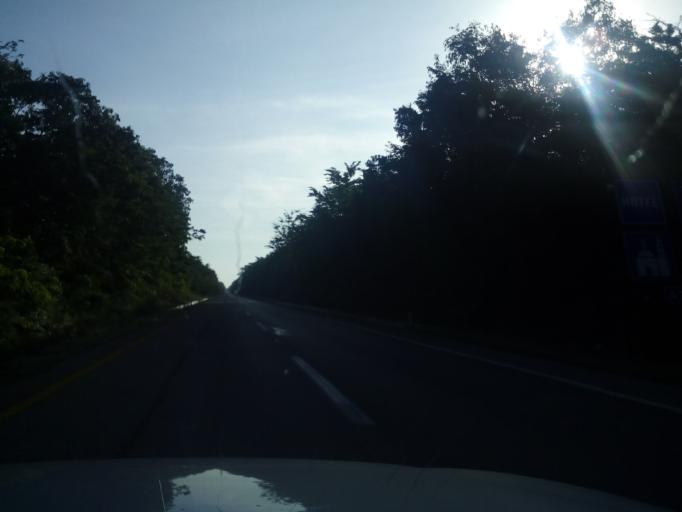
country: MX
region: Yucatan
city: Tinum
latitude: 20.7089
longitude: -88.4503
